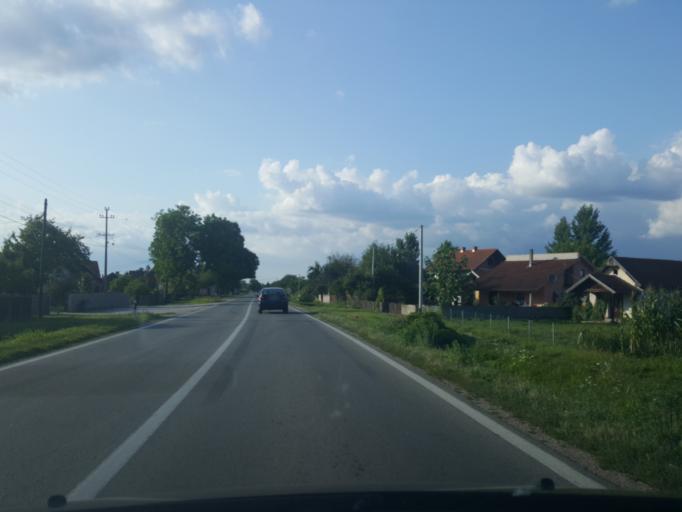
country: RS
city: Lipnicki Sor
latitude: 44.5925
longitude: 19.2582
